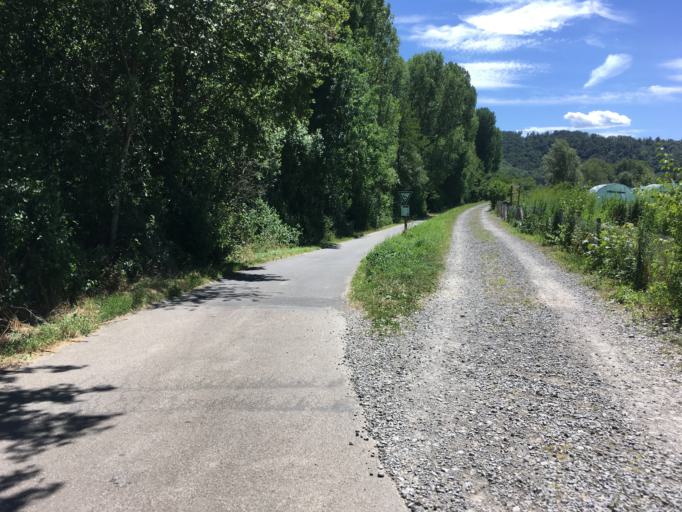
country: DE
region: Baden-Wuerttemberg
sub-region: Karlsruhe Region
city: Illingen
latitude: 48.9347
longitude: 8.9178
